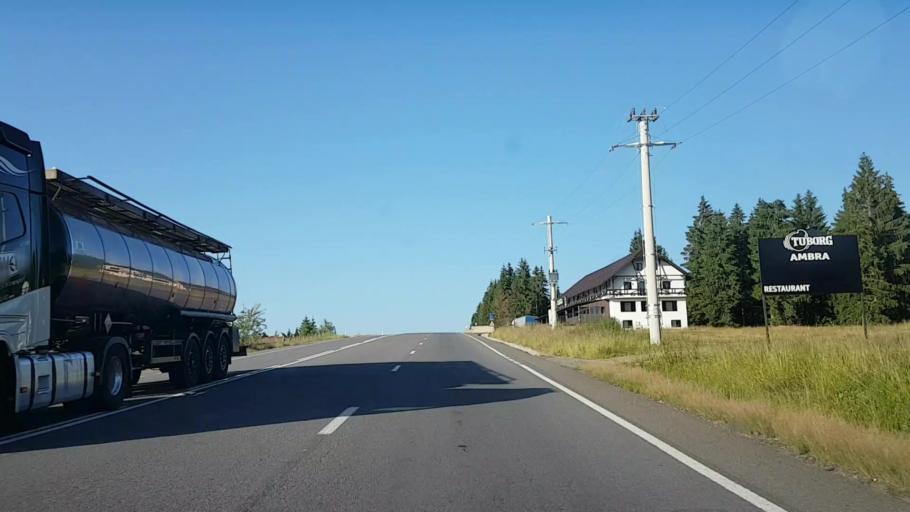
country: RO
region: Bistrita-Nasaud
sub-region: Comuna Lunca Ilvei
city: Lunca Ilvei
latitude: 47.2320
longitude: 24.9833
